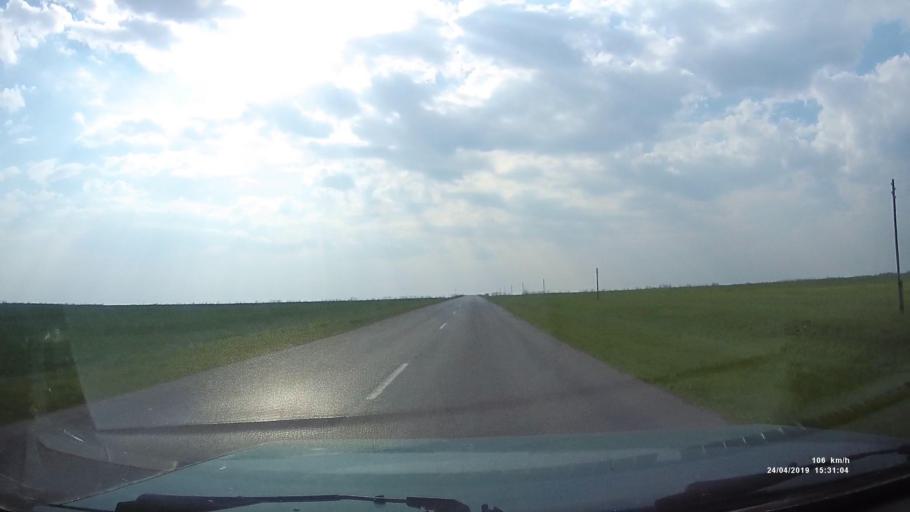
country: RU
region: Rostov
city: Remontnoye
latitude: 46.5998
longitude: 42.9919
